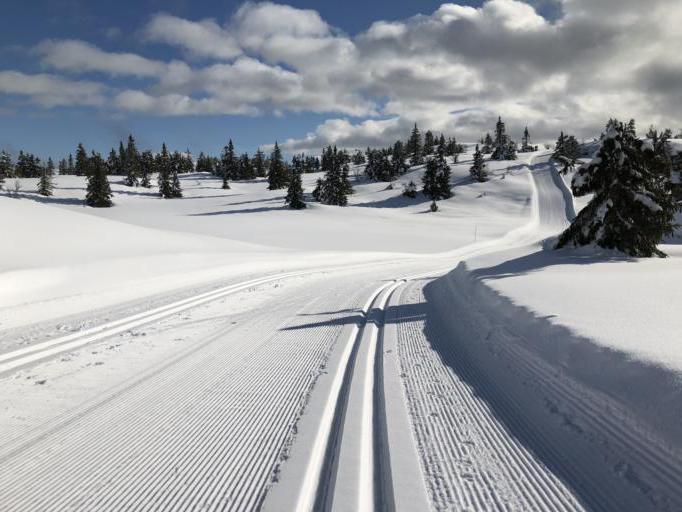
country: NO
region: Oppland
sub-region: Gausdal
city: Segalstad bru
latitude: 61.3299
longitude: 10.0335
